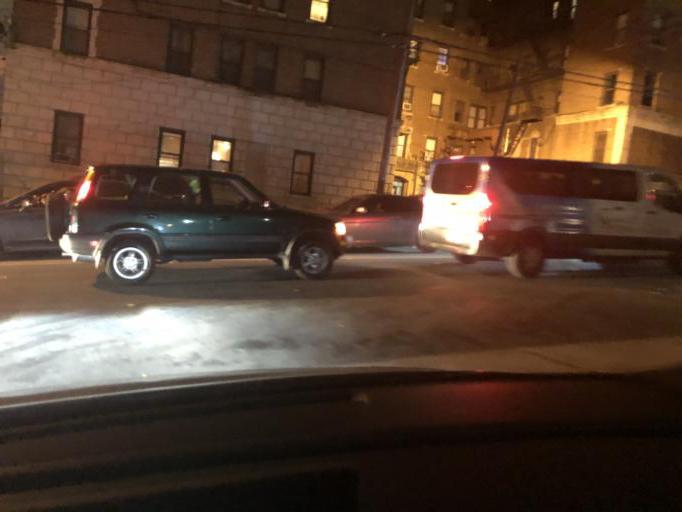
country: US
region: New Jersey
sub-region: Hudson County
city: East Newark
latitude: 40.7624
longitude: -74.1715
